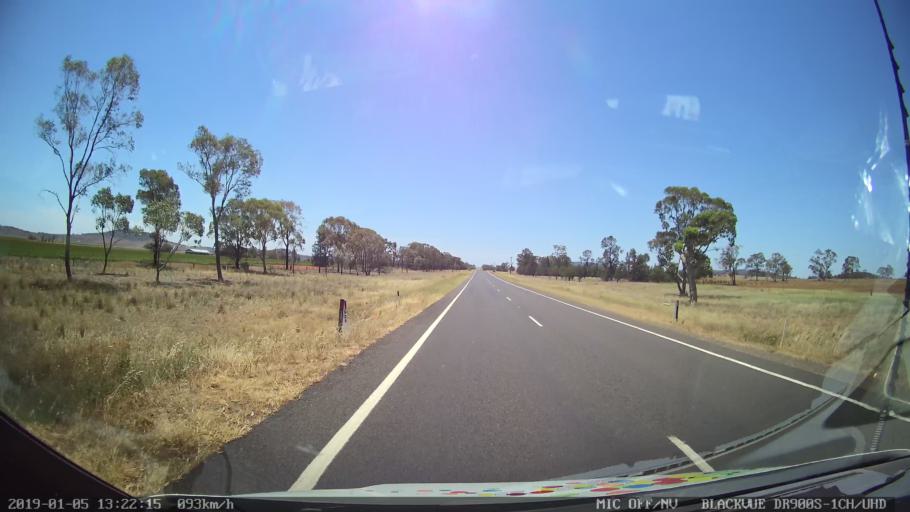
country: AU
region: New South Wales
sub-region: Gunnedah
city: Gunnedah
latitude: -31.0878
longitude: 149.9593
